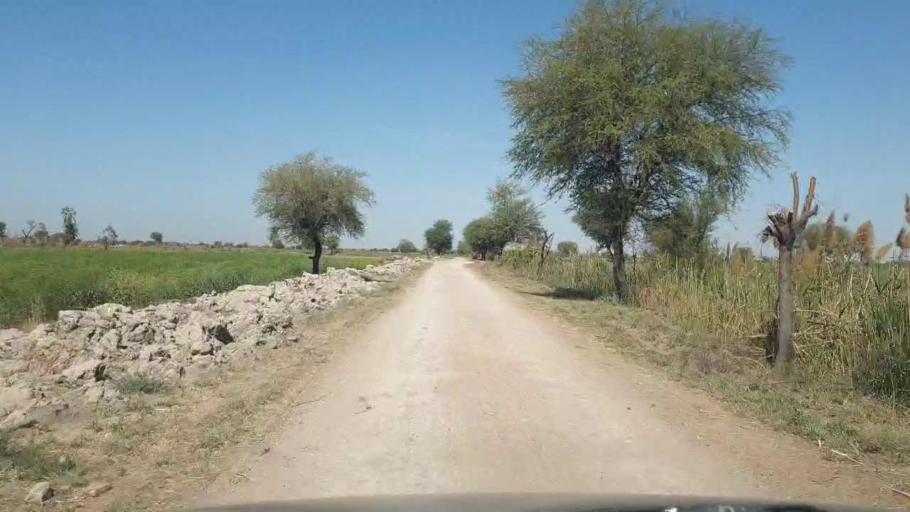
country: PK
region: Sindh
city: Dhoro Naro
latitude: 25.4470
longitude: 69.6156
